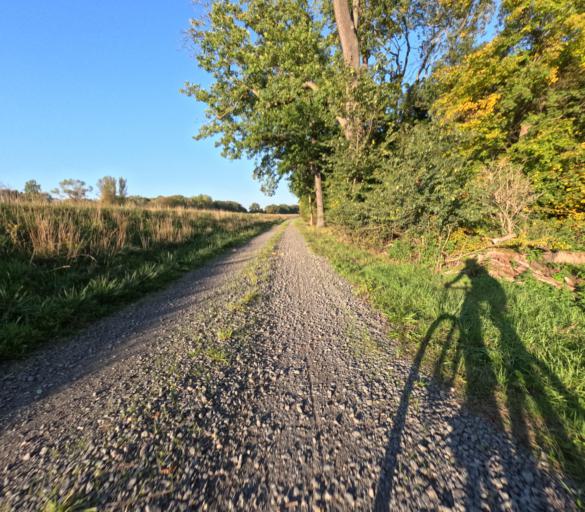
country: DE
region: Saxony
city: Schkeuditz
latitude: 51.3769
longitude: 12.2486
